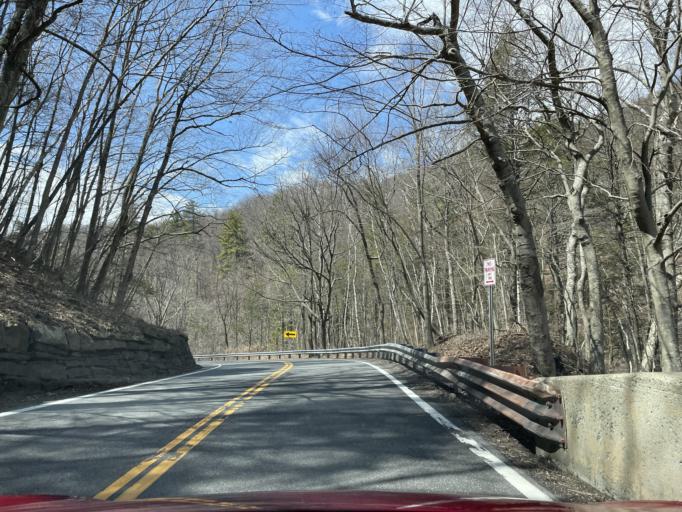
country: US
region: New York
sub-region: Greene County
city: Palenville
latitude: 42.1776
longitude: -74.0498
